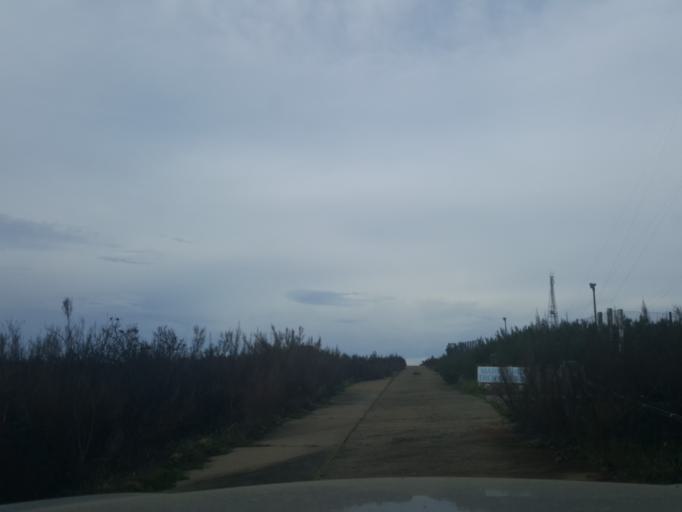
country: ZA
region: Limpopo
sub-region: Mopani District Municipality
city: Hoedspruit
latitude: -24.5448
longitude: 30.8658
